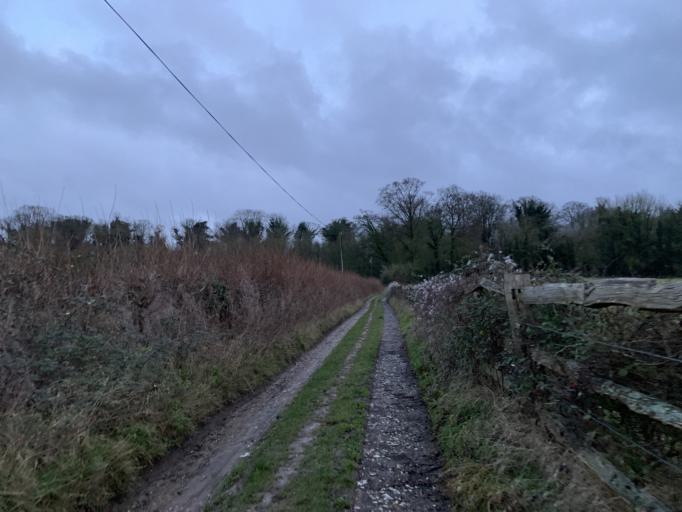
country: GB
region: England
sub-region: Kent
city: Eynsford
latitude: 51.3618
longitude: 0.2009
